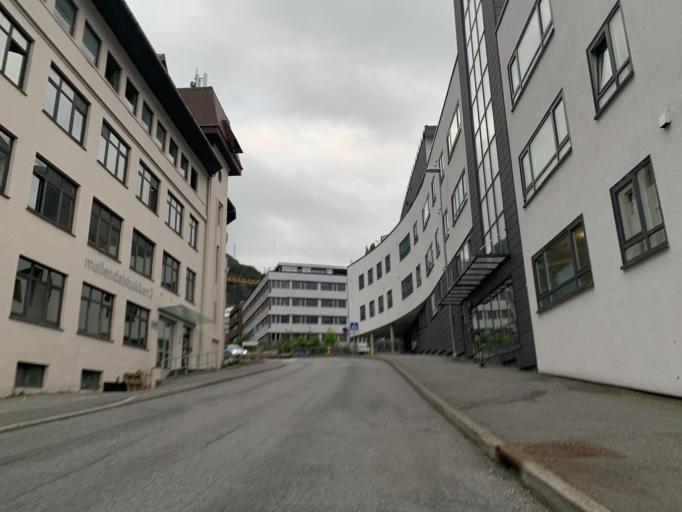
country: NO
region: Hordaland
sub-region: Bergen
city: Bergen
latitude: 60.3782
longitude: 5.3540
